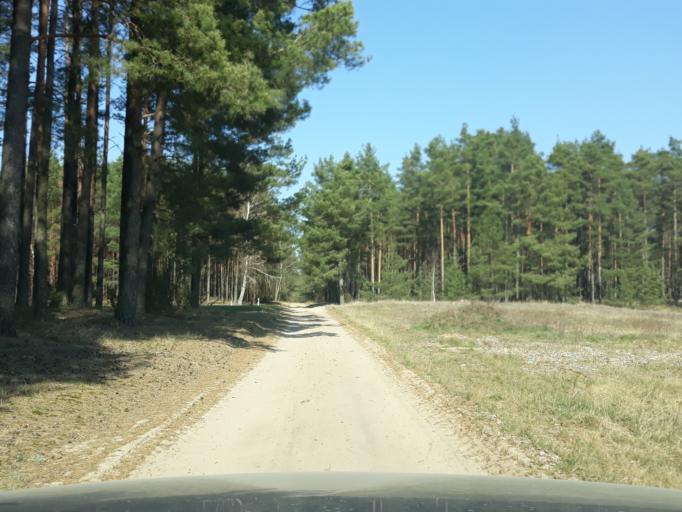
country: PL
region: Pomeranian Voivodeship
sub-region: Powiat bytowski
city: Lipnica
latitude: 53.8507
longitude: 17.4306
